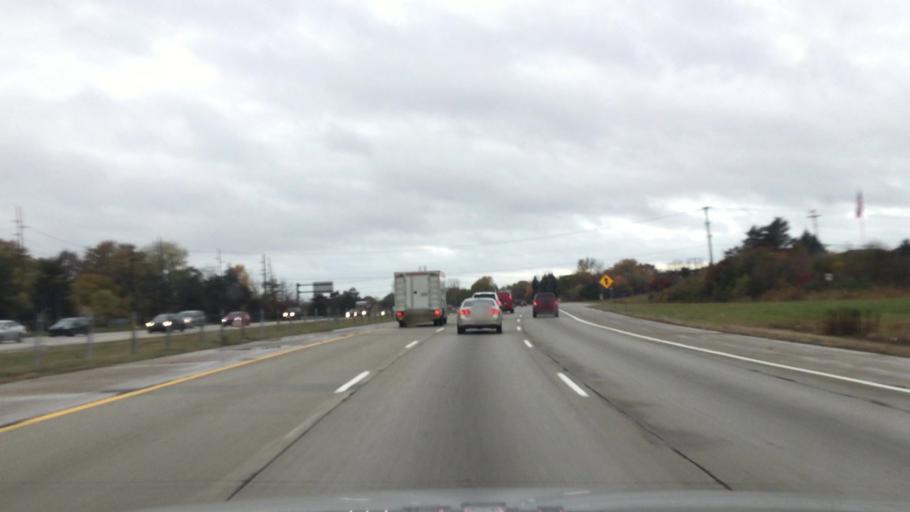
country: US
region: Michigan
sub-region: Wayne County
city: Belleville
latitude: 42.2206
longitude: -83.4428
